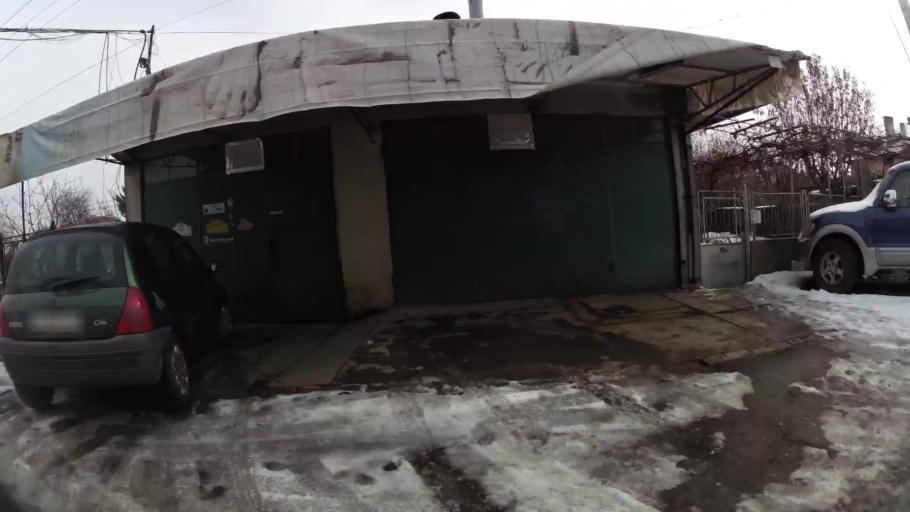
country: BG
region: Sofia-Capital
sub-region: Stolichna Obshtina
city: Sofia
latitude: 42.7152
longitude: 23.4000
